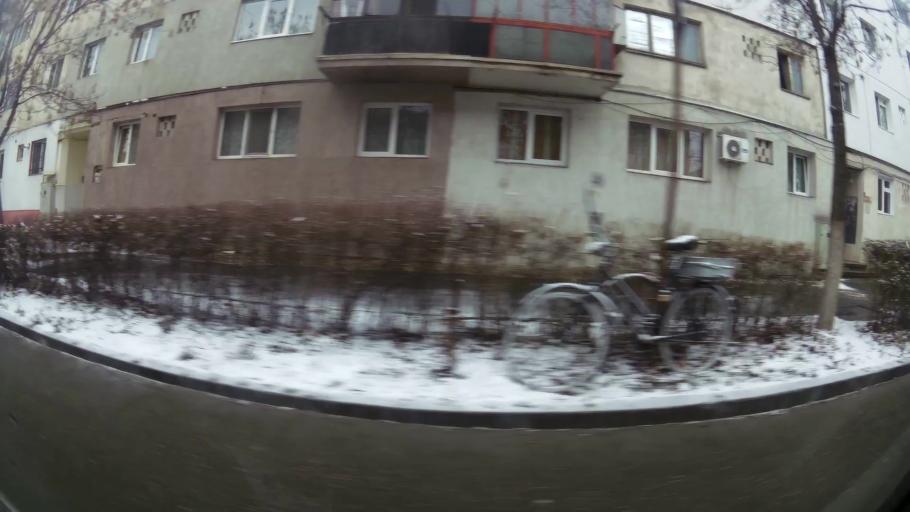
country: RO
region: Prahova
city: Ploiesti
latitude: 44.9328
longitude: 25.9970
